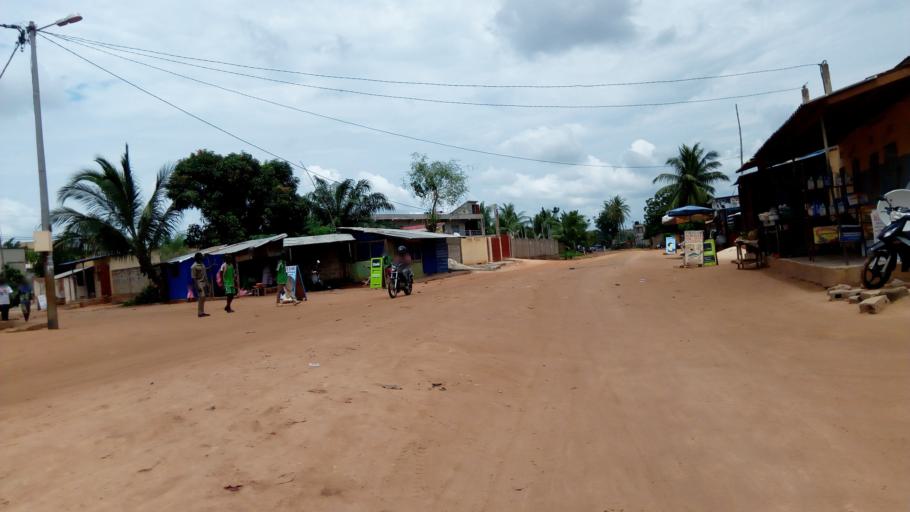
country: TG
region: Maritime
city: Lome
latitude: 6.2281
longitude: 1.1545
